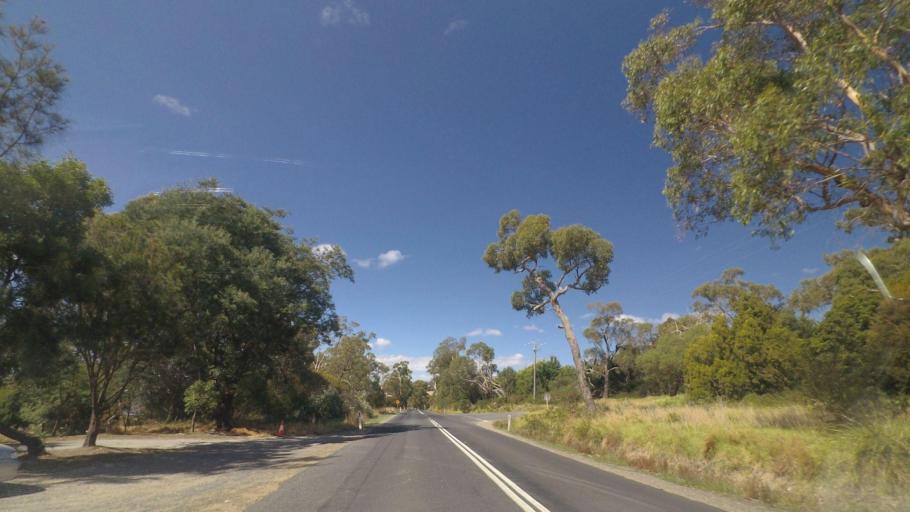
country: AU
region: Victoria
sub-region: Cardinia
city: Bunyip
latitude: -38.2455
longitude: 145.6905
